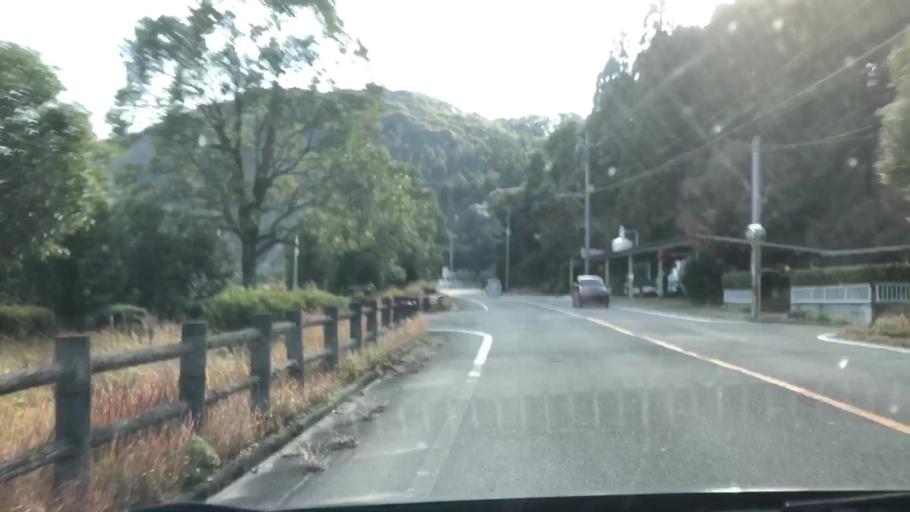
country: JP
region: Kagoshima
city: Satsumasendai
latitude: 31.8592
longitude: 130.3164
